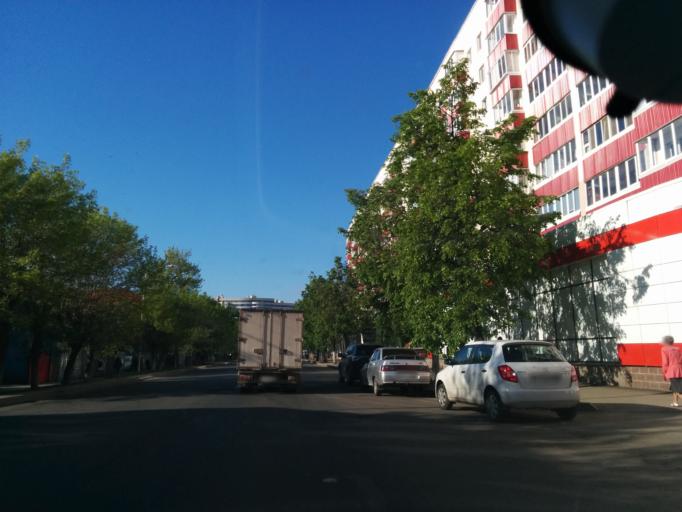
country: RU
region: Bashkortostan
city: Ufa
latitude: 54.7232
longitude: 55.9333
